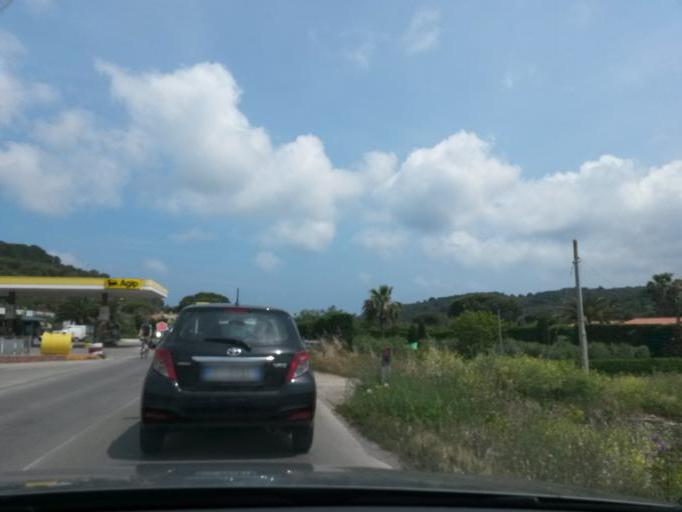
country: IT
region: Tuscany
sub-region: Provincia di Livorno
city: Capoliveri
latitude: 42.7590
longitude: 10.3770
